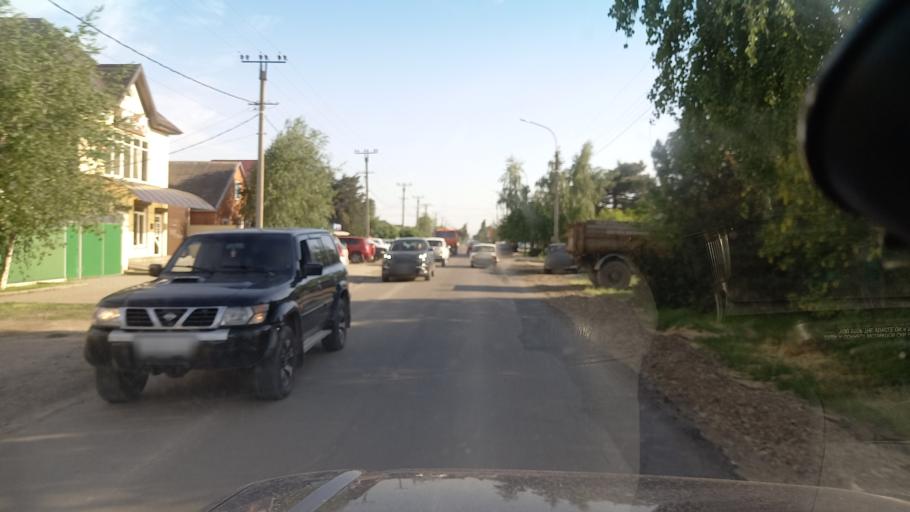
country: RU
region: Krasnodarskiy
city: Yelizavetinskaya
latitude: 45.0515
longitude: 38.7935
